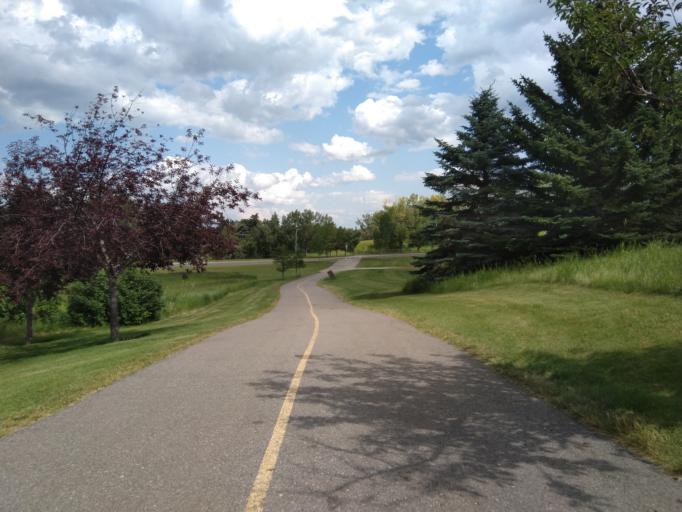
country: CA
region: Alberta
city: Calgary
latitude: 51.0789
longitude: -114.1084
